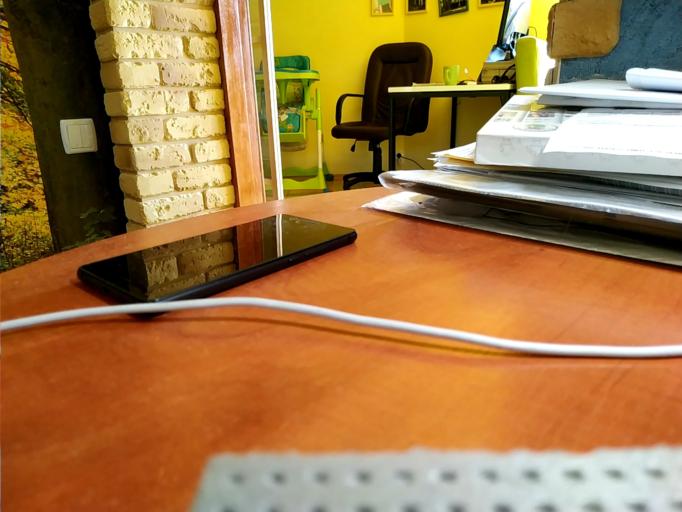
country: RU
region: Tverskaya
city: Kalashnikovo
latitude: 57.3806
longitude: 35.3520
